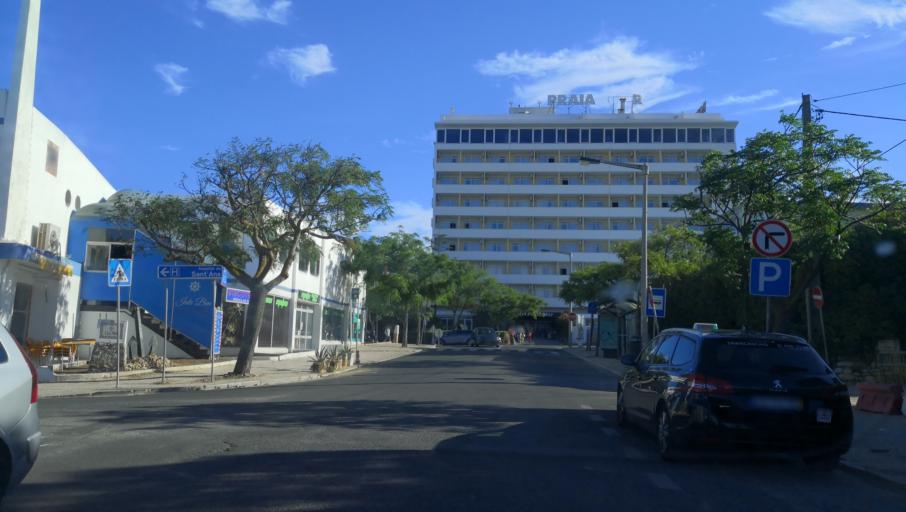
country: PT
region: Lisbon
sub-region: Cascais
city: Parede
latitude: 38.6824
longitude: -9.3423
